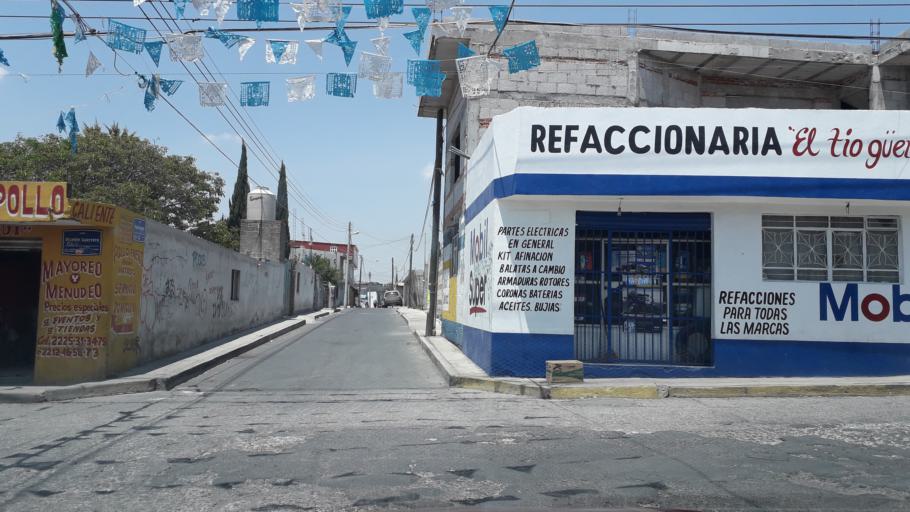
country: MX
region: Puebla
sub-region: Puebla
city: Santa Maria Xonacatepec
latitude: 19.0889
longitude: -98.1024
